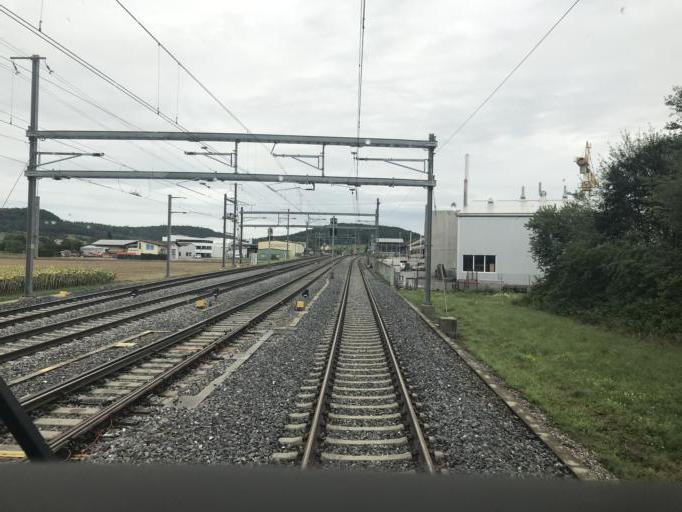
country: CH
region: Zurich
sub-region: Bezirk Buelach
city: Rafz
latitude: 47.6004
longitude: 8.5382
